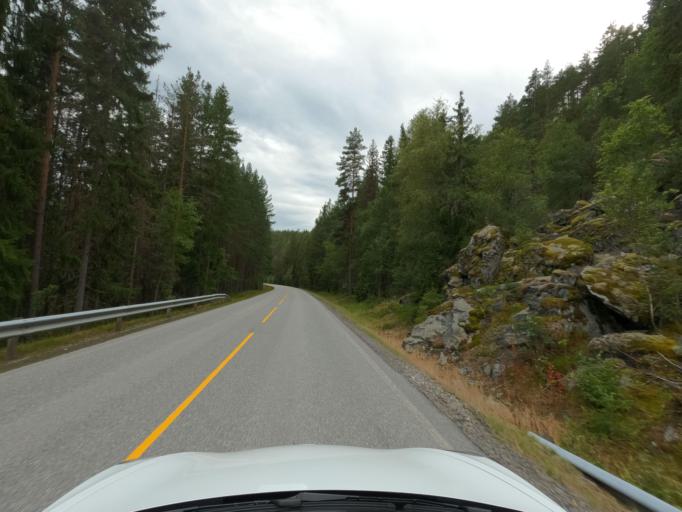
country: NO
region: Telemark
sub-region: Hjartdal
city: Sauland
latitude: 59.7339
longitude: 9.0184
